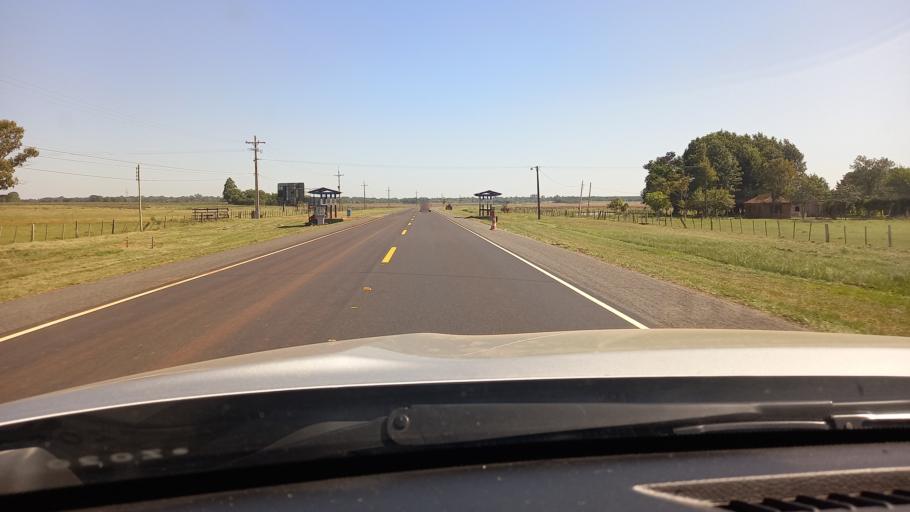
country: PY
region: Itapua
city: General Delgado
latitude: -27.0837
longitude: -56.5542
